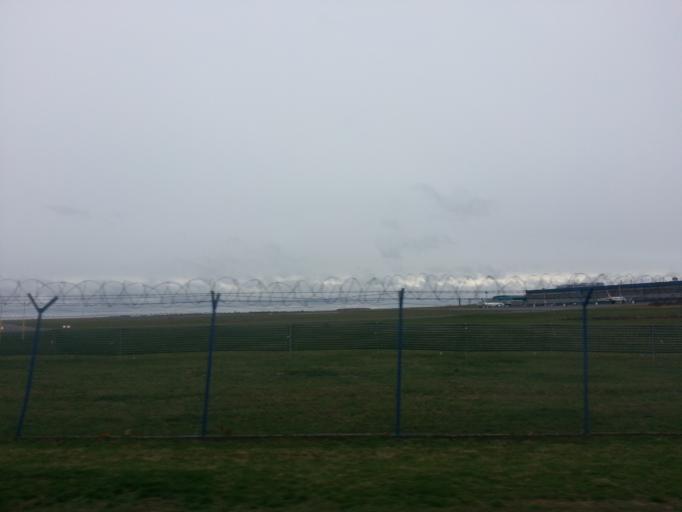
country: CZ
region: Central Bohemia
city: Tuchomerice
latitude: 50.1056
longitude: 14.2874
